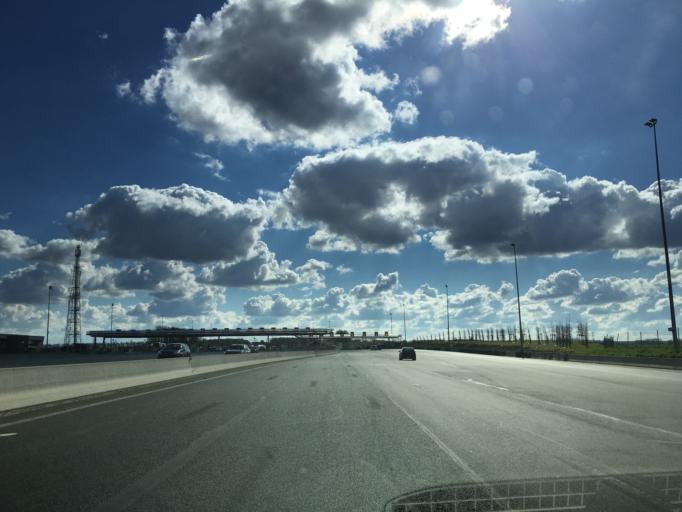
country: FR
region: Nord-Pas-de-Calais
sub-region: Departement du Pas-de-Calais
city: Roeux
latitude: 50.3270
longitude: 2.9137
